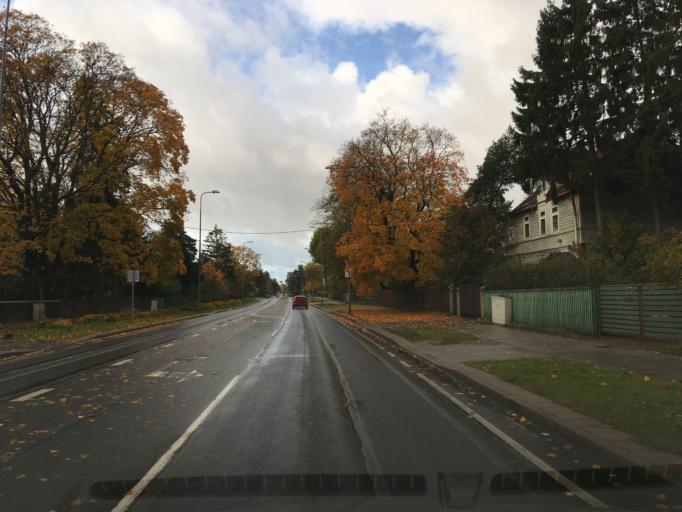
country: EE
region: Harju
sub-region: Saue vald
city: Laagri
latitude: 59.3774
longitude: 24.6519
